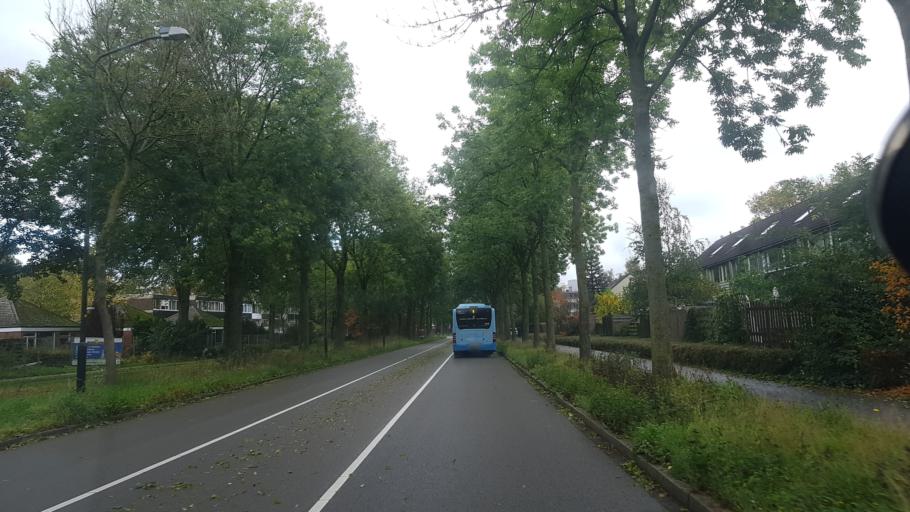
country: NL
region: Gelderland
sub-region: Gemeente Apeldoorn
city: Apeldoorn
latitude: 52.2227
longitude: 5.9809
